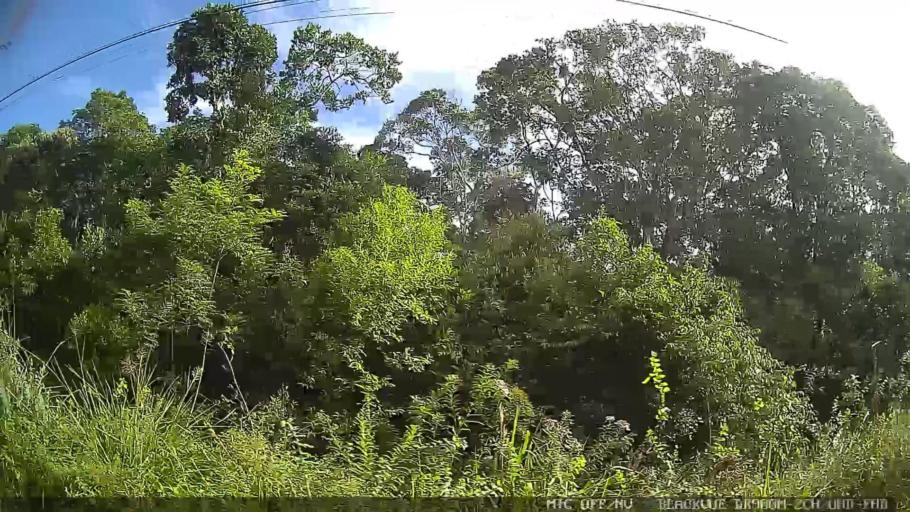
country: BR
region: Sao Paulo
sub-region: Itanhaem
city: Itanhaem
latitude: -24.2065
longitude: -46.8830
